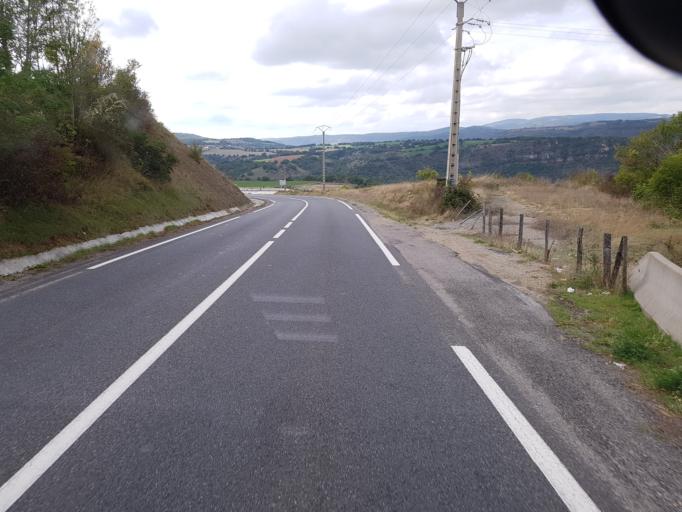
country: FR
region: Midi-Pyrenees
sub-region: Departement de l'Aveyron
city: Saint-Georges-de-Luzencon
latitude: 44.0798
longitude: 3.0005
